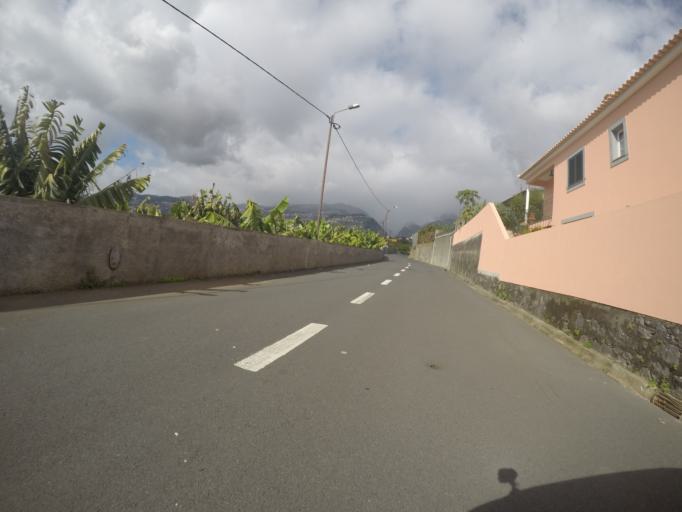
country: PT
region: Madeira
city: Camara de Lobos
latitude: 32.6485
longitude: -16.9517
